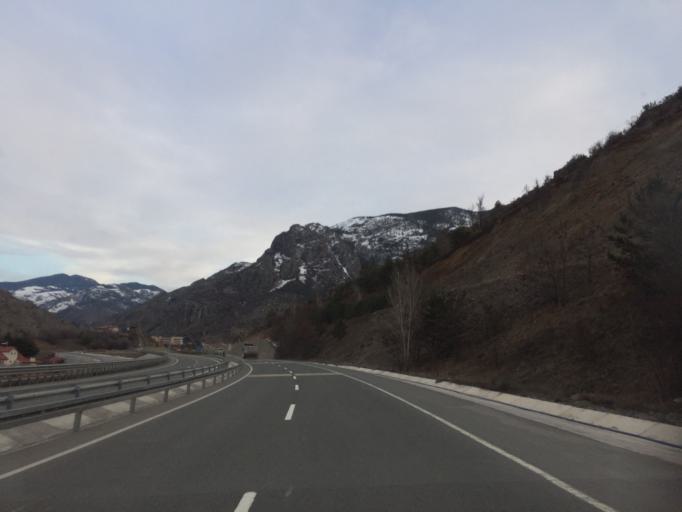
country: TR
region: Gumushane
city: Gumushkhane
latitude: 40.5050
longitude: 39.4240
